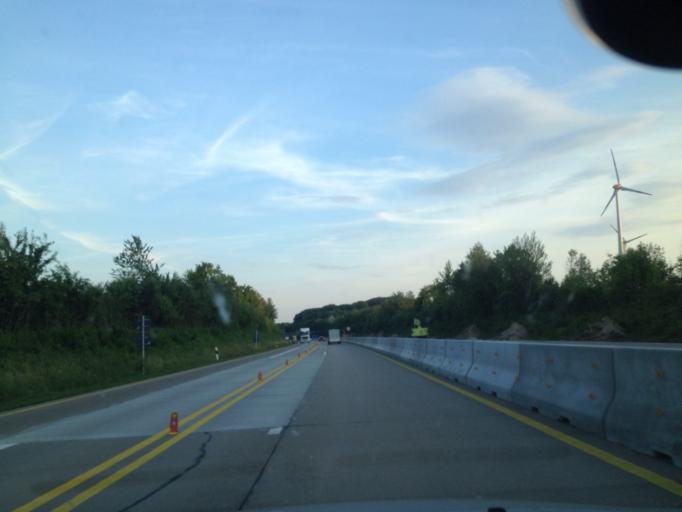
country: DE
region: Bavaria
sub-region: Regierungsbezirk Mittelfranken
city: Gollhofen
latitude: 49.5842
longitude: 10.1719
